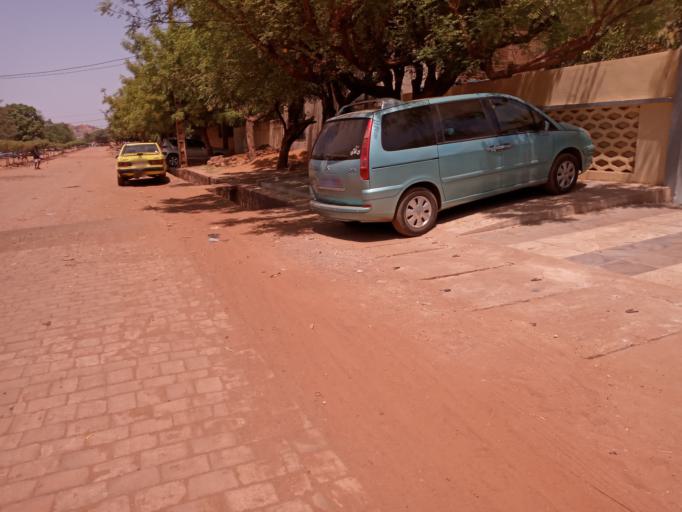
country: ML
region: Bamako
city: Bamako
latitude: 12.6642
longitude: -7.9495
